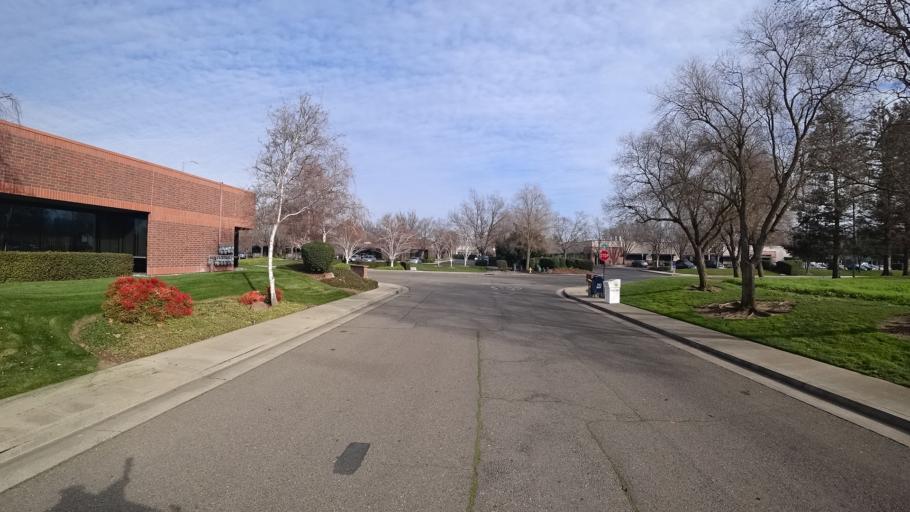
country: US
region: California
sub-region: Yolo County
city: Davis
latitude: 38.5421
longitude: -121.7277
